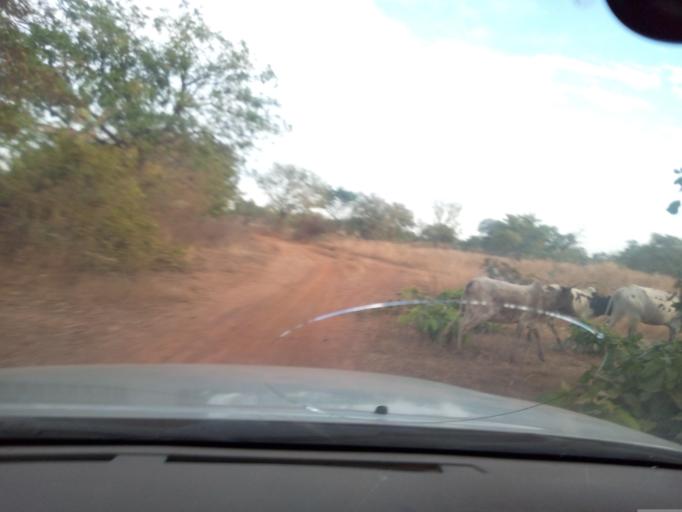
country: ML
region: Sikasso
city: Kadiolo
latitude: 10.5827
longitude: -5.8426
